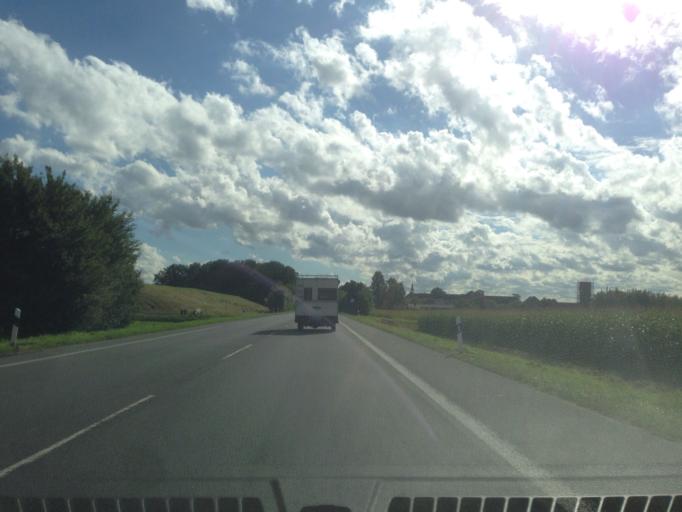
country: DE
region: North Rhine-Westphalia
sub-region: Regierungsbezirk Munster
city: Senden
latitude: 51.8816
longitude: 7.5688
